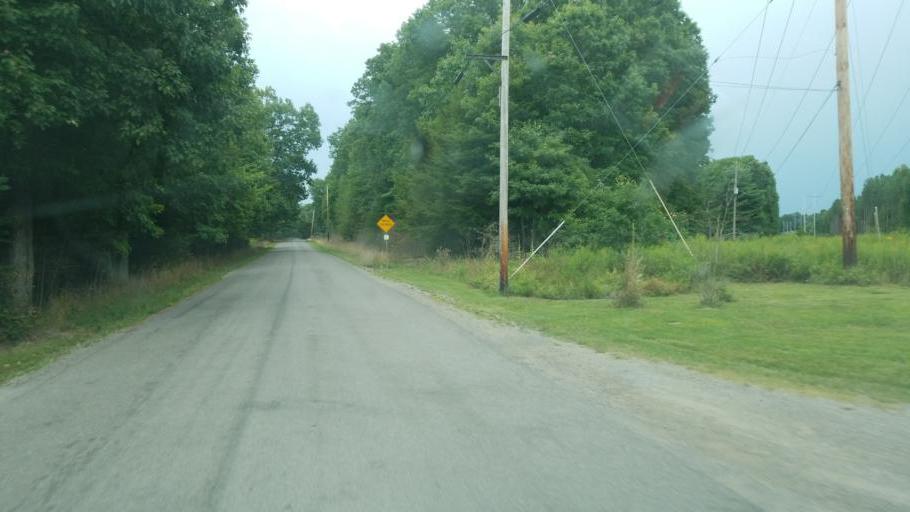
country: US
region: Pennsylvania
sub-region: Clarion County
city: Marianne
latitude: 41.2037
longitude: -79.4460
